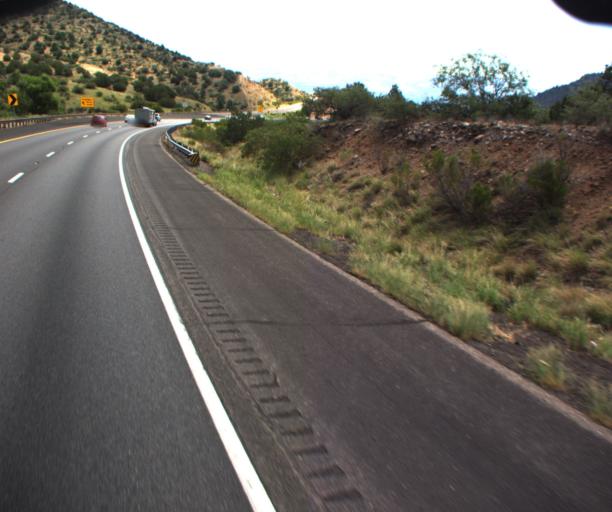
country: US
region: Arizona
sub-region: Yavapai County
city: Camp Verde
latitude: 34.5372
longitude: -111.9260
